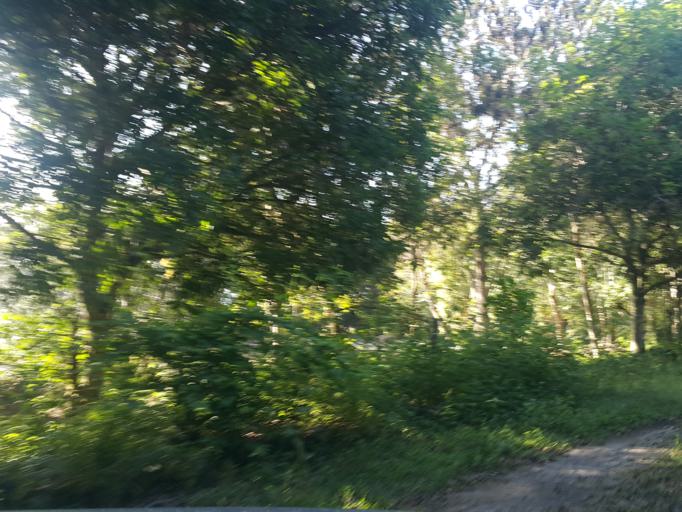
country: TH
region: Chiang Mai
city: Mae On
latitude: 18.7028
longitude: 99.2077
